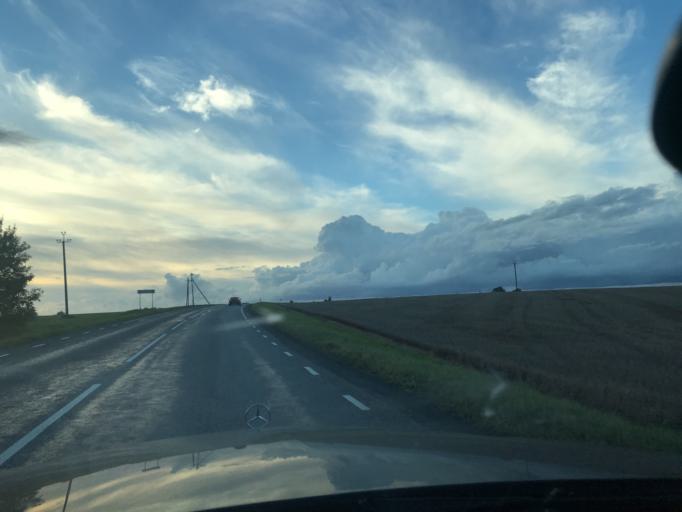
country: EE
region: Vorumaa
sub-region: Antsla vald
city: Vana-Antsla
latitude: 57.8811
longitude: 26.5422
